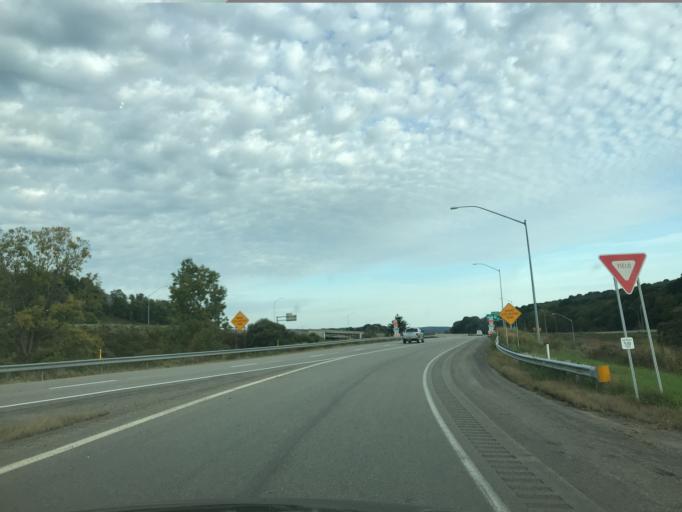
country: US
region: Pennsylvania
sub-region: Crawford County
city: Meadville
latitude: 41.6239
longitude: -80.1839
